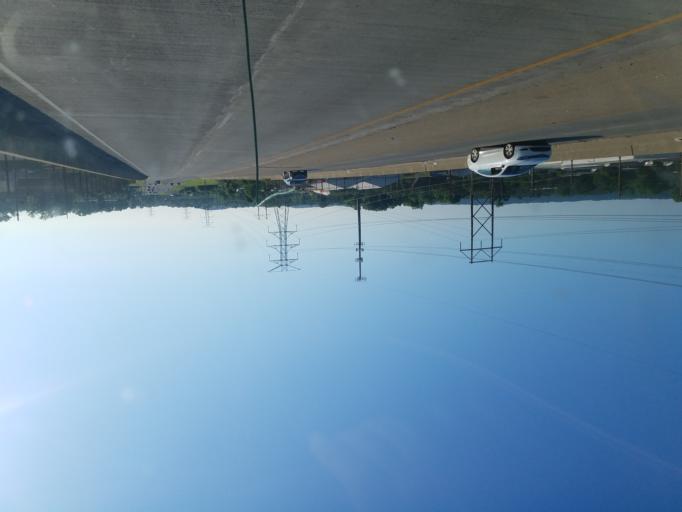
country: US
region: Kentucky
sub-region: Jefferson County
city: Heritage Creek
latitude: 38.1288
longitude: -85.7414
